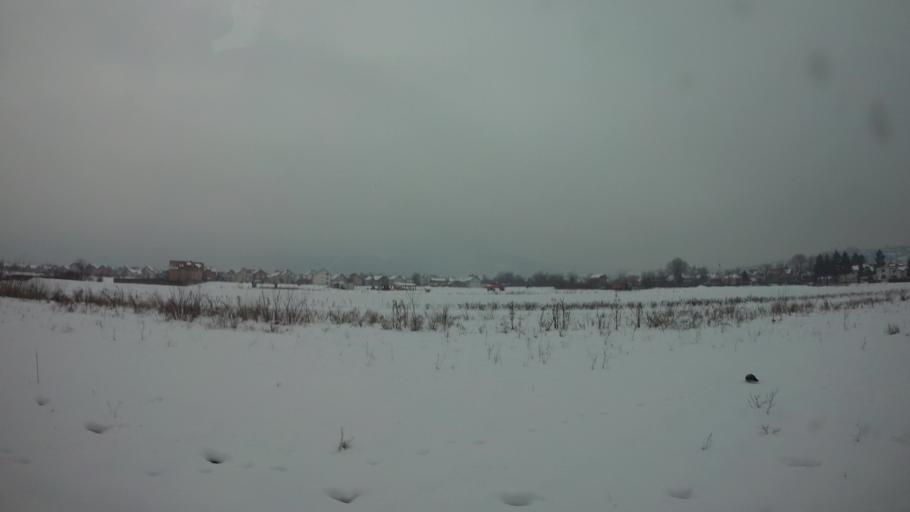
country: BA
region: Federation of Bosnia and Herzegovina
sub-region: Kanton Sarajevo
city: Sarajevo
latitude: 43.8424
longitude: 18.2860
